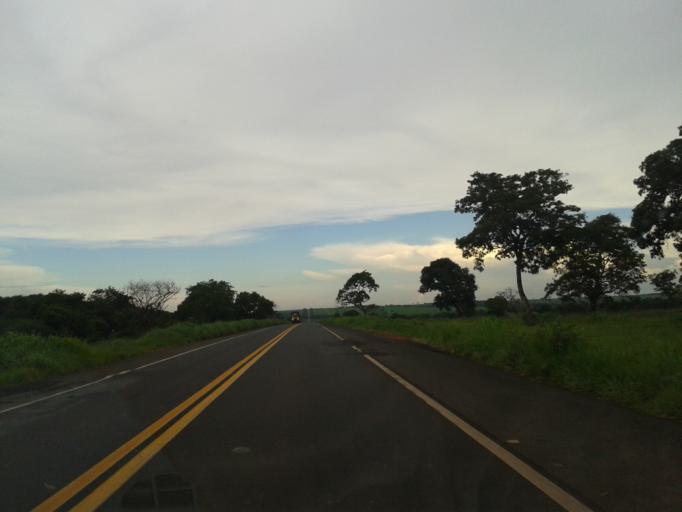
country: BR
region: Minas Gerais
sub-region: Santa Vitoria
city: Santa Vitoria
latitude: -18.9121
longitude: -50.2235
